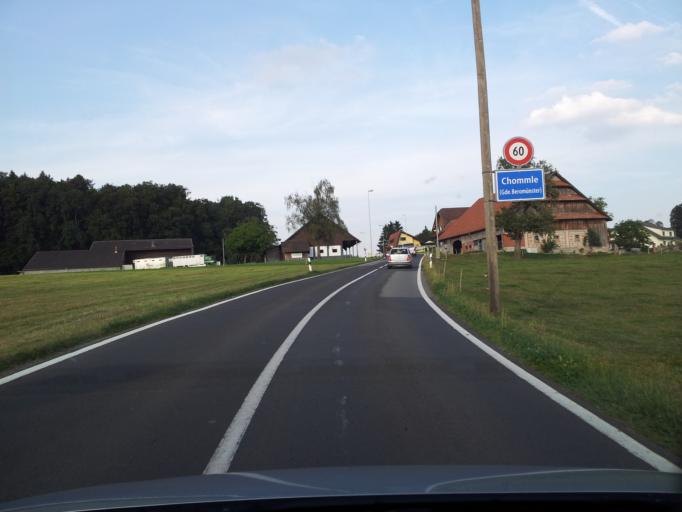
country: CH
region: Lucerne
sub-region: Sursee District
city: Schenkon
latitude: 47.1918
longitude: 8.1552
